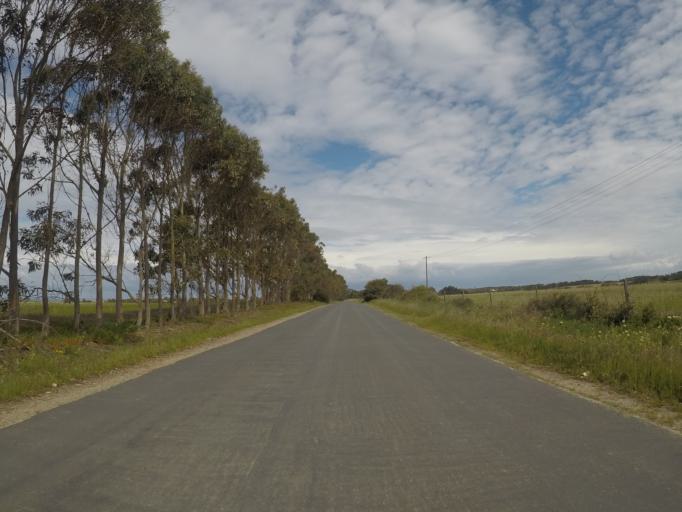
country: PT
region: Beja
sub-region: Odemira
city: Sao Teotonio
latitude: 37.4914
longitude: -8.7816
